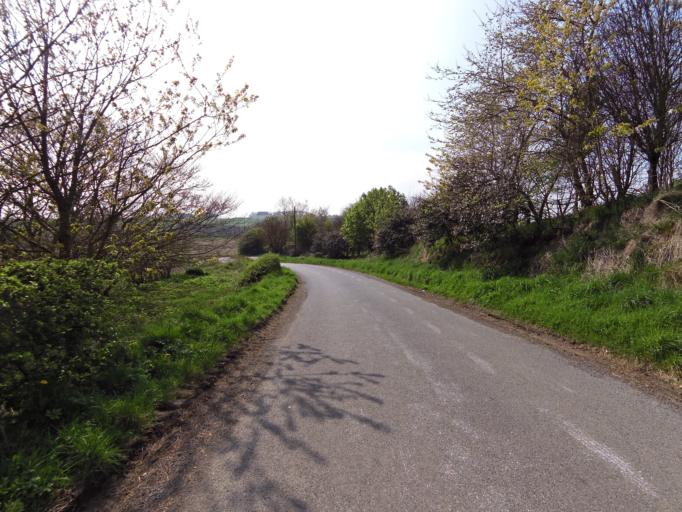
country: GB
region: Scotland
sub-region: Fife
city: Kinghorn
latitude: 56.0753
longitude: -3.1850
